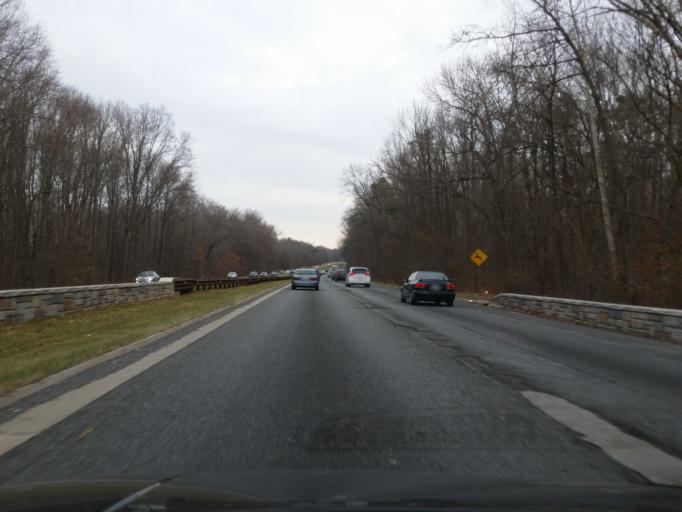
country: US
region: Maryland
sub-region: Prince George's County
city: South Laurel
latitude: 39.0701
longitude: -76.8306
